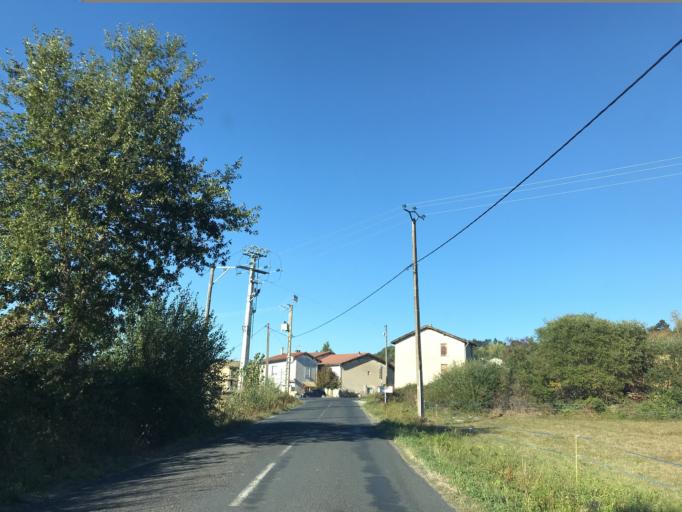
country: FR
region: Auvergne
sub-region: Departement du Puy-de-Dome
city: Escoutoux
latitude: 45.7766
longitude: 3.5919
